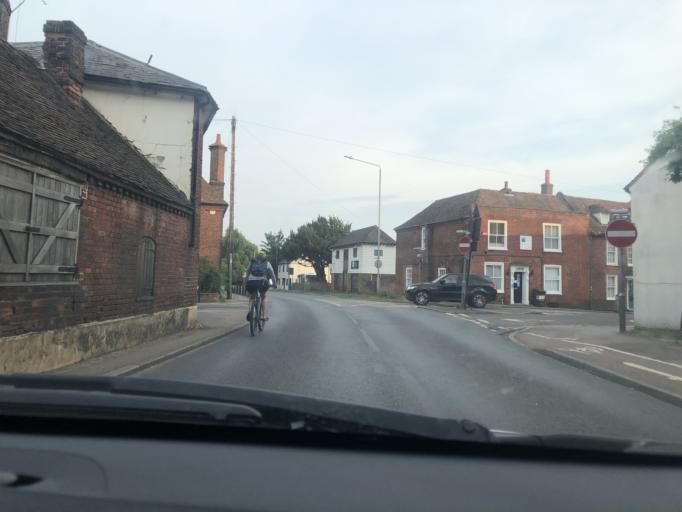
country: GB
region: England
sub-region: Kent
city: Sturry
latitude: 51.3008
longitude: 1.1220
